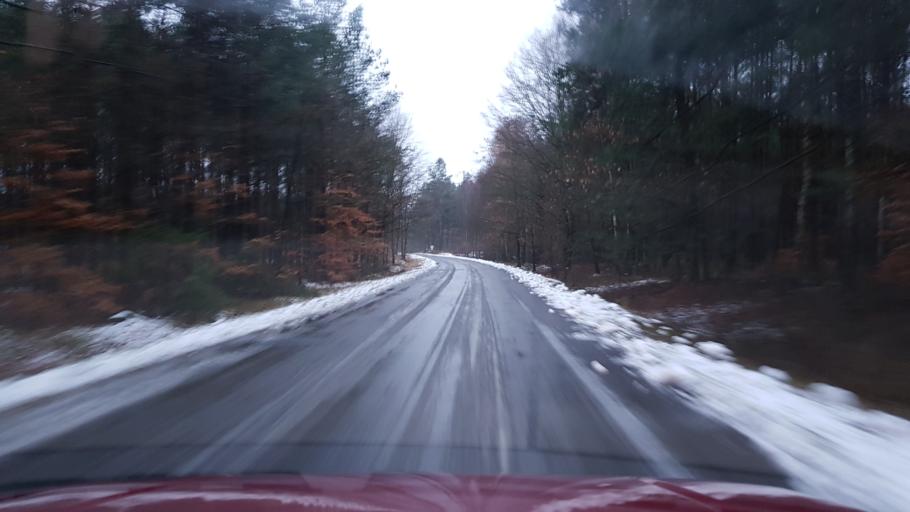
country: PL
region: West Pomeranian Voivodeship
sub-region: Powiat goleniowski
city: Goleniow
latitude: 53.4942
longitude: 14.8768
